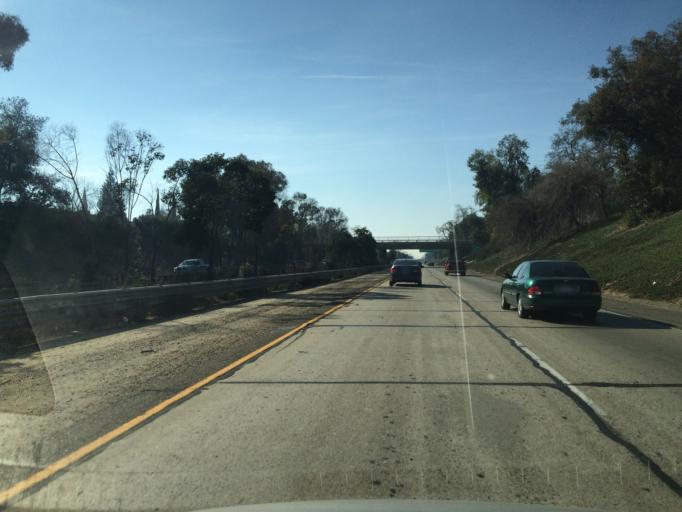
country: US
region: California
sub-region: Tulare County
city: Visalia
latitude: 36.3271
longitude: -119.3033
